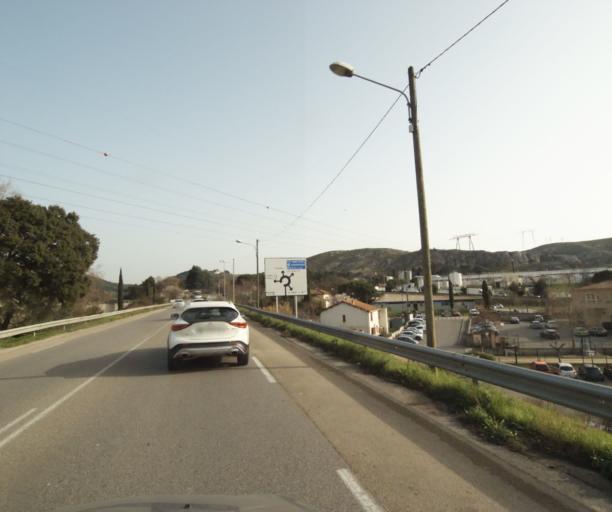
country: FR
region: Provence-Alpes-Cote d'Azur
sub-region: Departement des Bouches-du-Rhone
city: Les Pennes-Mirabeau
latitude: 43.4107
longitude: 5.3230
